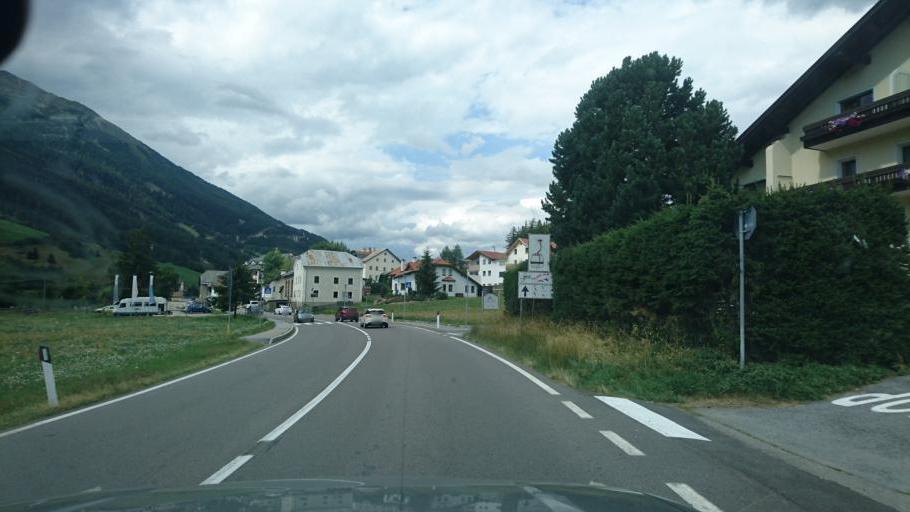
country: IT
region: Trentino-Alto Adige
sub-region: Bolzano
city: Curon Venosta
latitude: 46.7586
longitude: 10.5376
